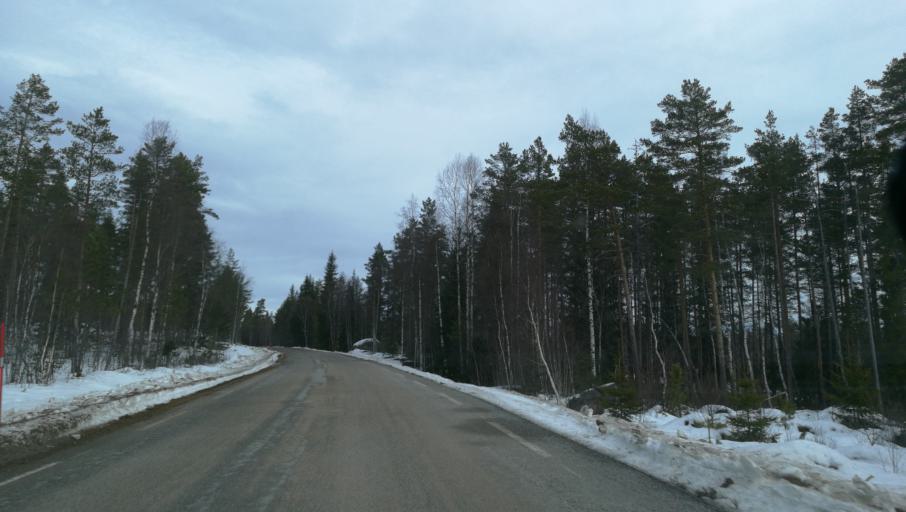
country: NO
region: Hedmark
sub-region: Grue
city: Kirkenaer
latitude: 60.5217
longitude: 12.5528
